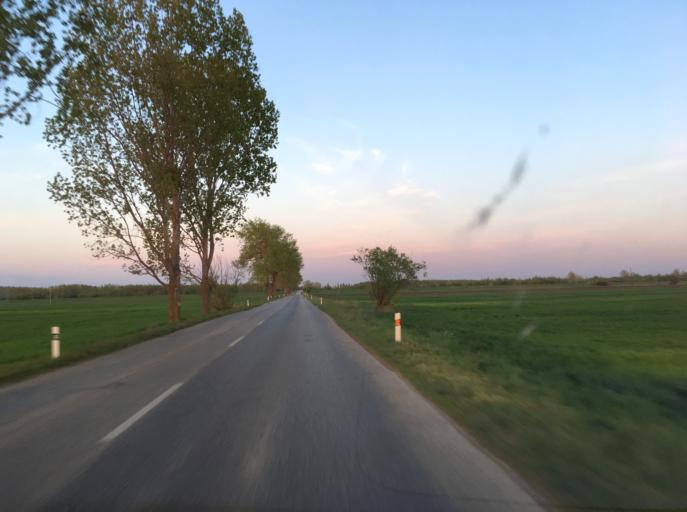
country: SK
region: Nitriansky
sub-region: Okres Nove Zamky
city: Nove Zamky
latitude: 47.9224
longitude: 18.0964
